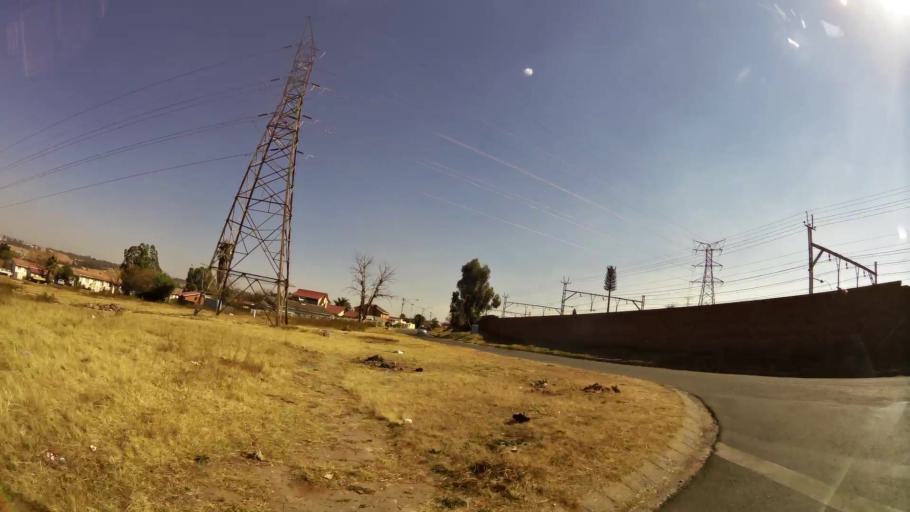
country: ZA
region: Gauteng
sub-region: City of Johannesburg Metropolitan Municipality
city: Johannesburg
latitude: -26.1867
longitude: 27.9594
